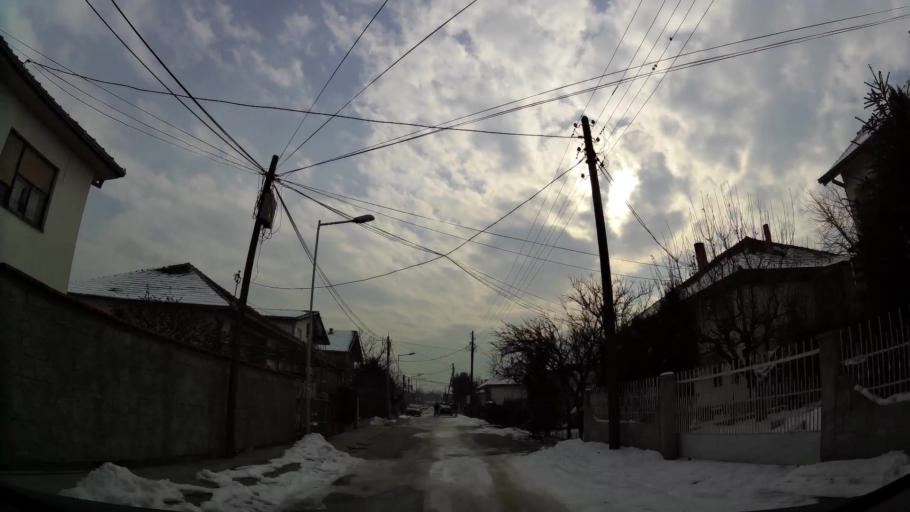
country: MK
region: Saraj
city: Saraj
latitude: 42.0170
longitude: 21.3532
